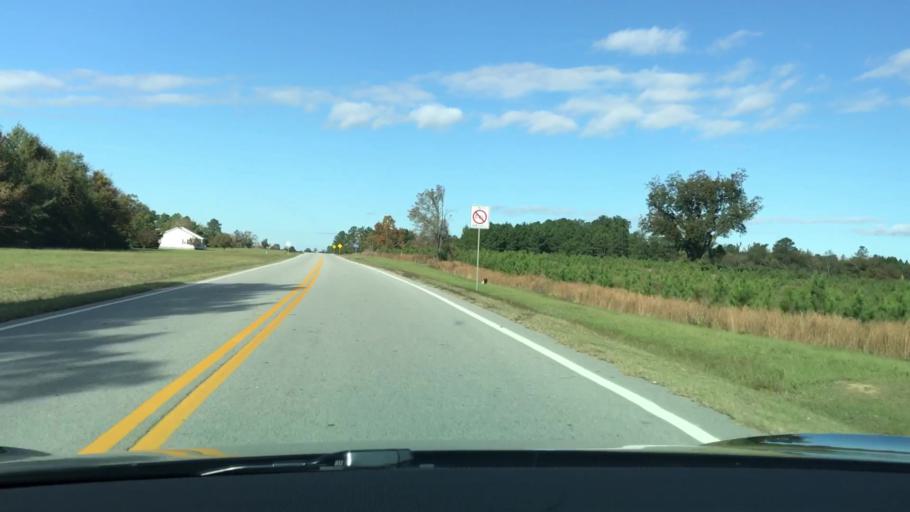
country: US
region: Georgia
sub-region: Jefferson County
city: Wrens
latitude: 33.2588
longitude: -82.4735
